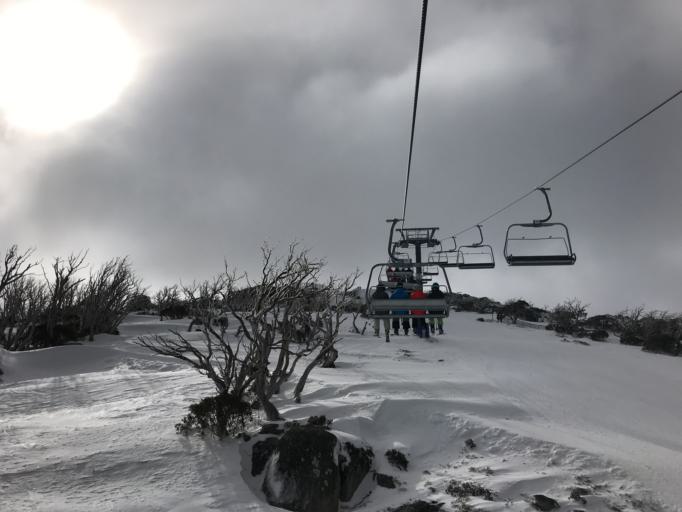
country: AU
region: New South Wales
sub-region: Snowy River
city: Jindabyne
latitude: -36.3829
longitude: 148.3831
